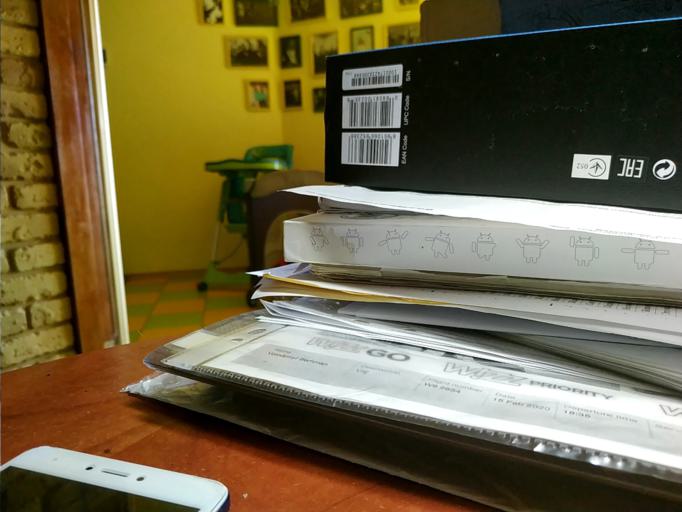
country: RU
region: Novgorod
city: Kholm
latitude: 59.2642
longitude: 32.7983
